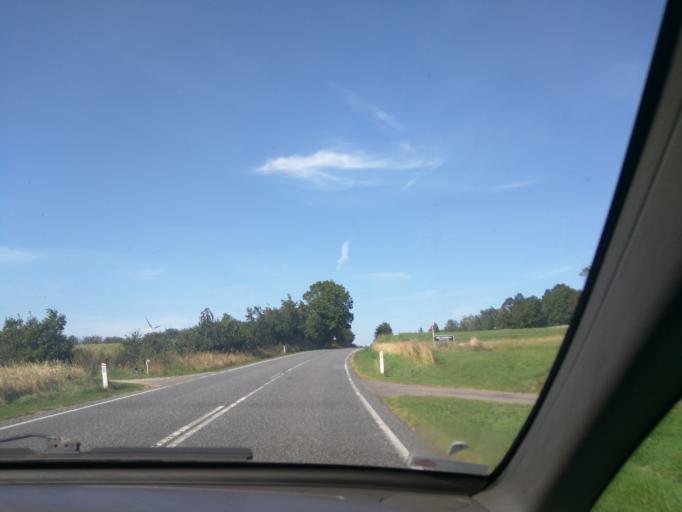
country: DK
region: Central Jutland
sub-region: Viborg Kommune
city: Bjerringbro
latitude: 56.4233
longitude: 9.6711
